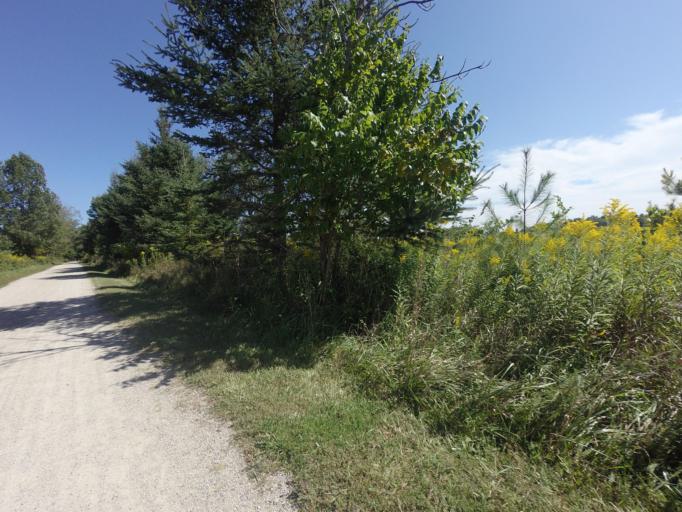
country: CA
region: Ontario
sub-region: Wellington County
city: Guelph
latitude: 43.7248
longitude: -80.3715
